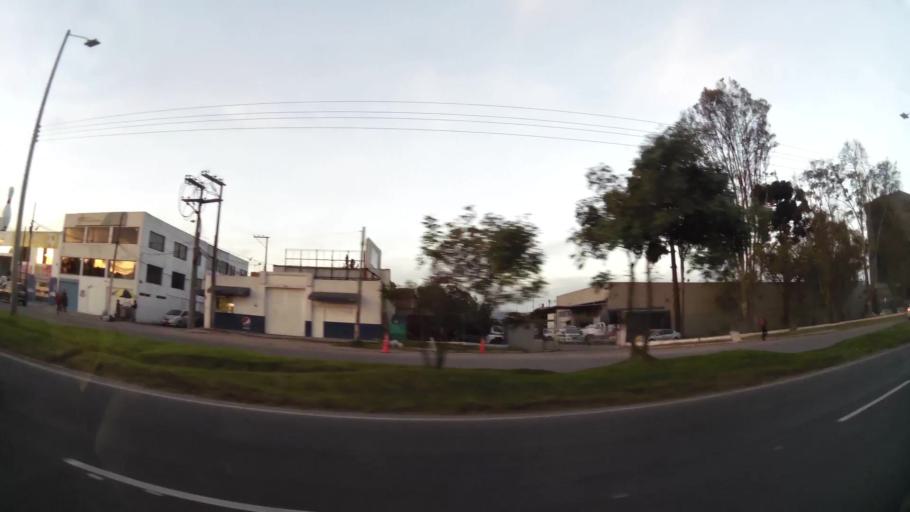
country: CO
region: Cundinamarca
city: Funza
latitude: 4.6882
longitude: -74.1289
